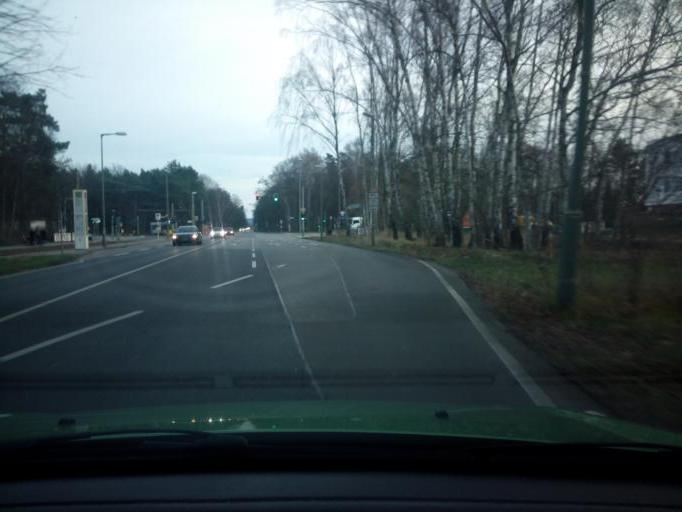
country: DE
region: Berlin
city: Berlin Koepenick
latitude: 52.4391
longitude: 13.5909
